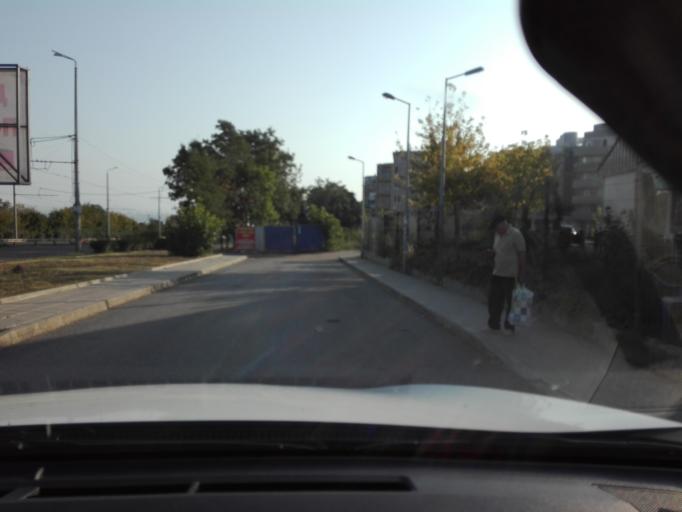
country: BG
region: Burgas
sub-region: Obshtina Burgas
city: Burgas
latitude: 42.4623
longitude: 27.4110
